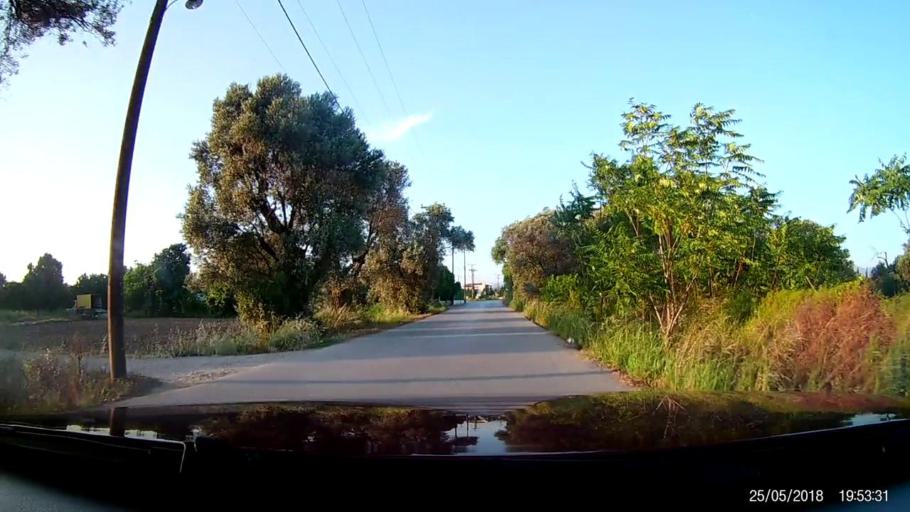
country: GR
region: Central Greece
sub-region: Nomos Evvoias
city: Ayios Nikolaos
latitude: 38.4175
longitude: 23.6510
